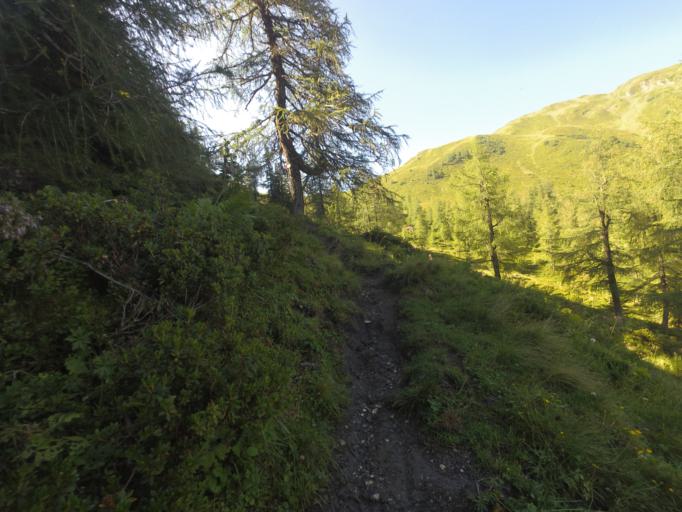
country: AT
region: Salzburg
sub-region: Politischer Bezirk Sankt Johann im Pongau
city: Dorfgastein
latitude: 47.2390
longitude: 13.0612
